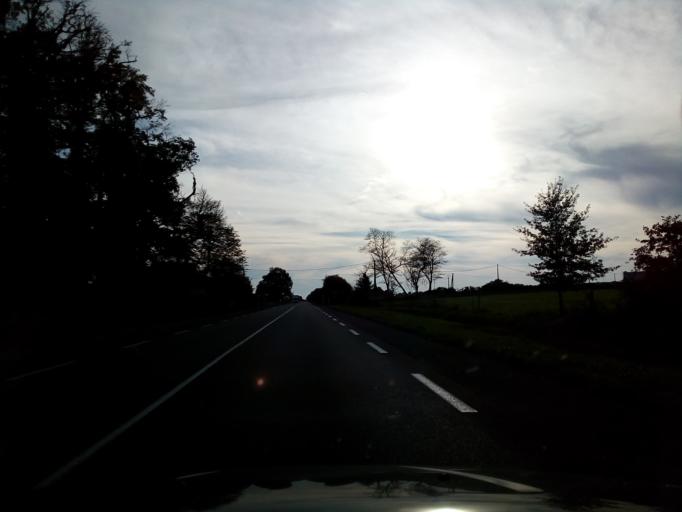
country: FR
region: Poitou-Charentes
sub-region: Departement de la Charente
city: Loubert
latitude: 45.9813
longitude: 0.6010
